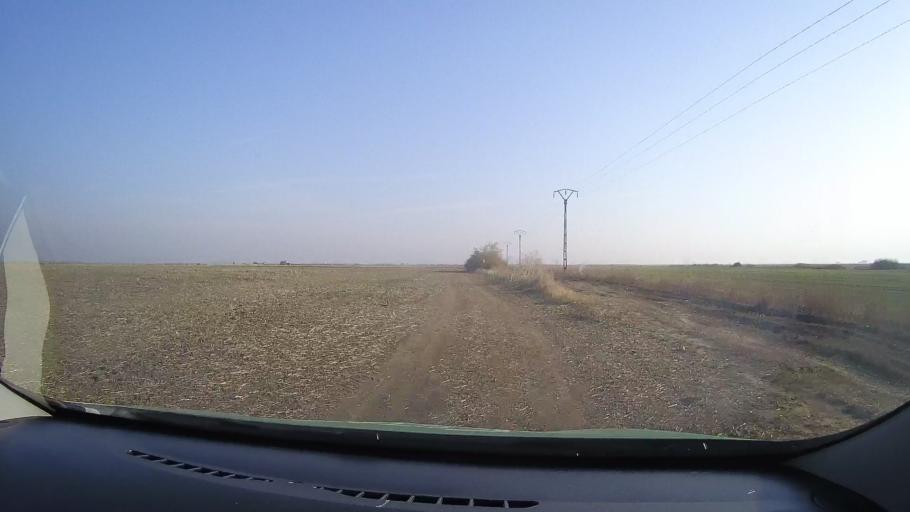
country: RO
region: Arad
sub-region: Comuna Graniceri
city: Graniceri
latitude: 46.5310
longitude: 21.3159
